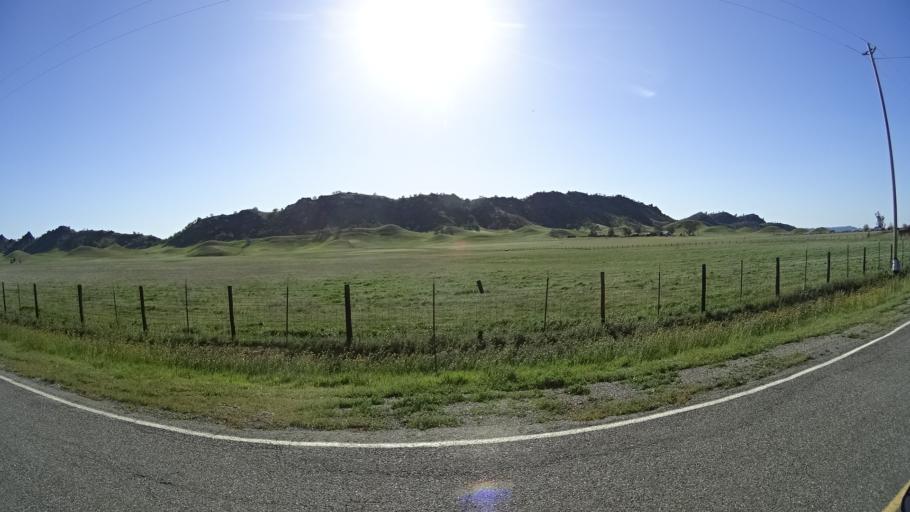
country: US
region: California
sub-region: Tehama County
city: Rancho Tehama Reserve
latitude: 39.7331
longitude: -122.5503
